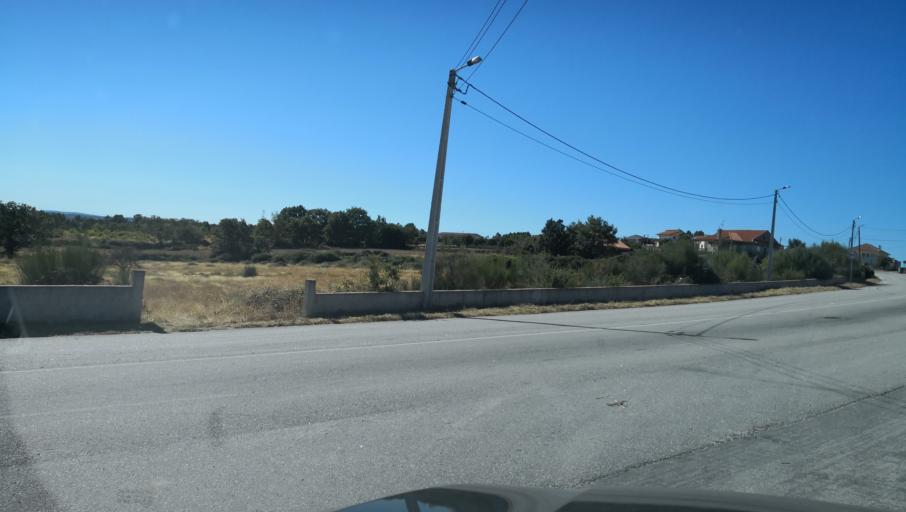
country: PT
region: Vila Real
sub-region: Valpacos
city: Valpacos
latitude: 41.6714
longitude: -7.3393
